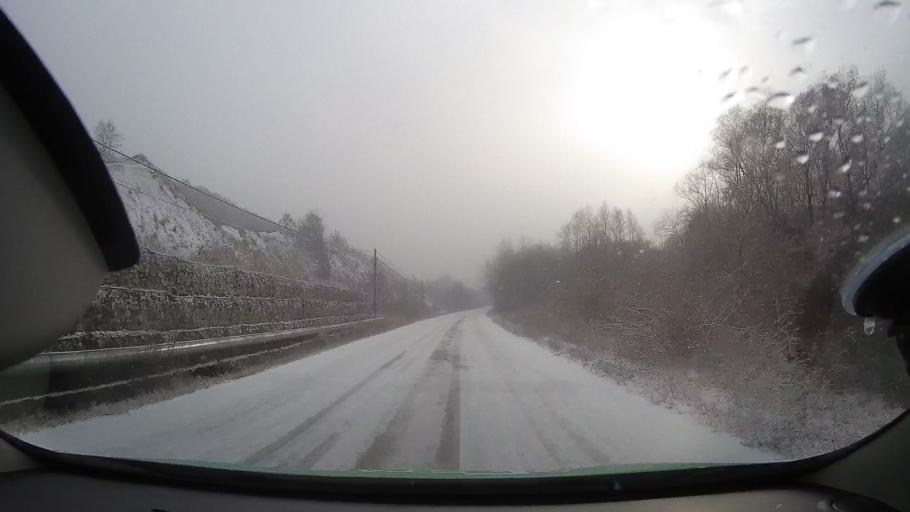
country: RO
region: Alba
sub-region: Comuna Livezile
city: Livezile
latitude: 46.3590
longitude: 23.6130
